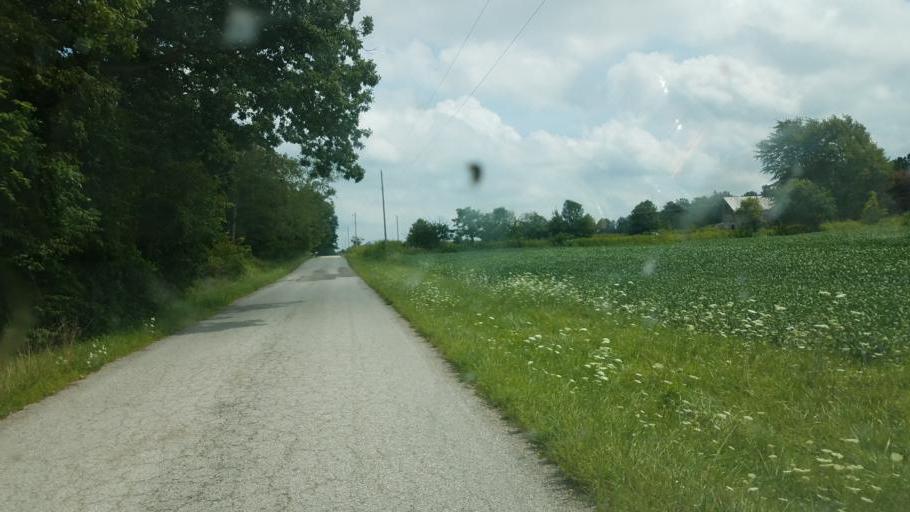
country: US
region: Ohio
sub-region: Richland County
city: Lexington
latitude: 40.6742
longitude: -82.6858
